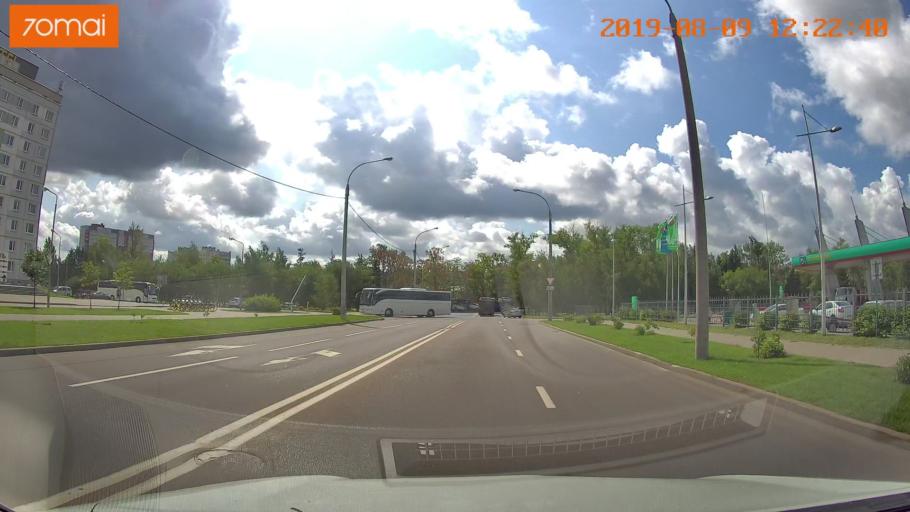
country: BY
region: Minsk
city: Zhdanovichy
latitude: 53.9321
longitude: 27.4744
